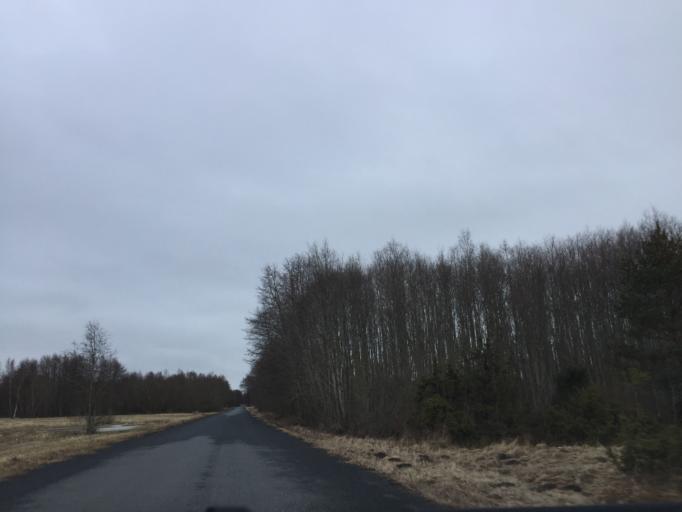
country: EE
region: Laeaene
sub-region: Haapsalu linn
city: Haapsalu
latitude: 58.7924
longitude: 23.4814
